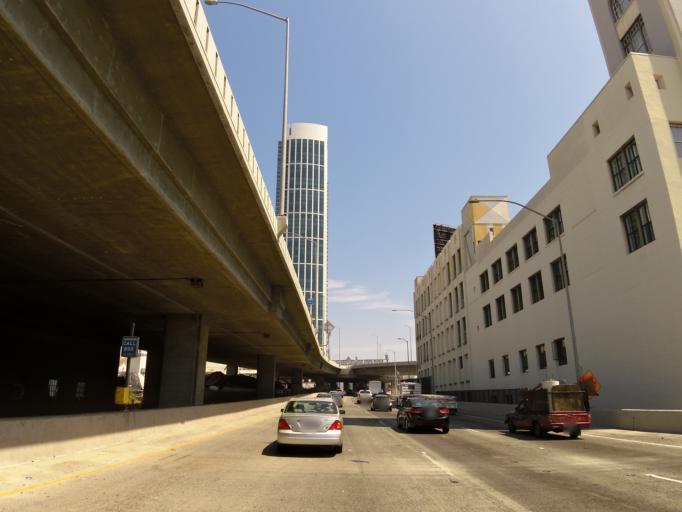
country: US
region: California
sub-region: San Francisco County
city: San Francisco
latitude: 37.7836
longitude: -122.3945
